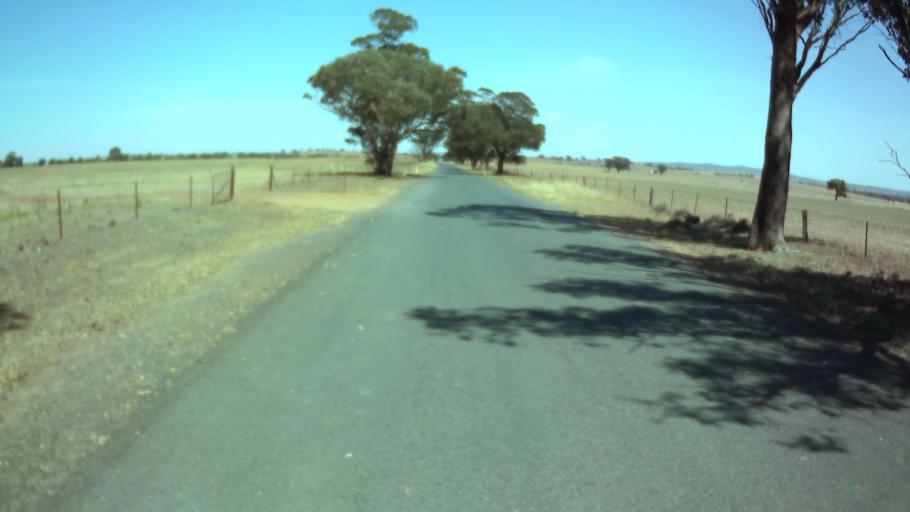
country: AU
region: New South Wales
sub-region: Weddin
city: Grenfell
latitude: -33.8589
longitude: 147.9688
